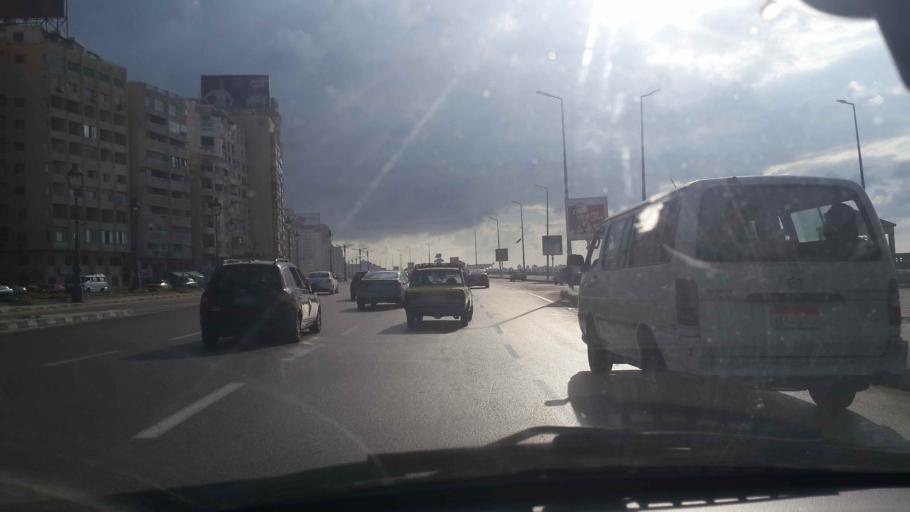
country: EG
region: Alexandria
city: Alexandria
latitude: 31.2203
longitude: 29.9295
